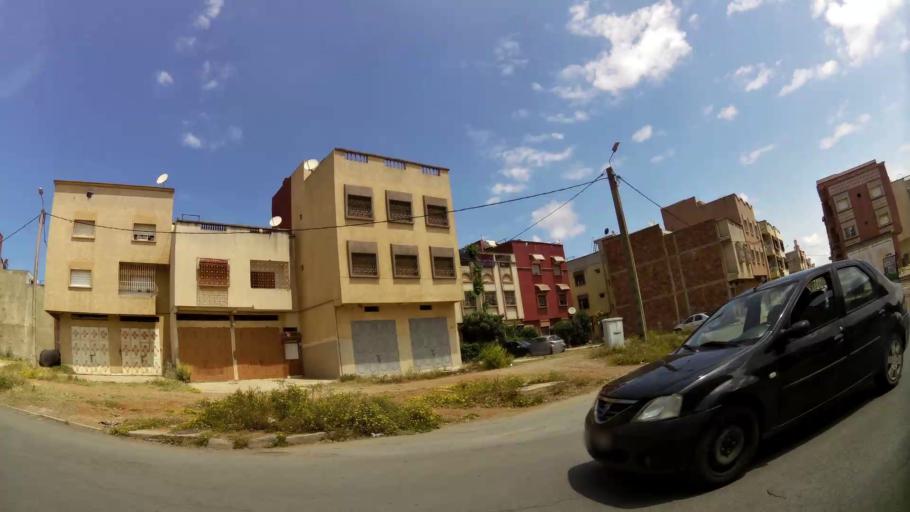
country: MA
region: Gharb-Chrarda-Beni Hssen
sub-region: Kenitra Province
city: Kenitra
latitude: 34.2658
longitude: -6.6084
